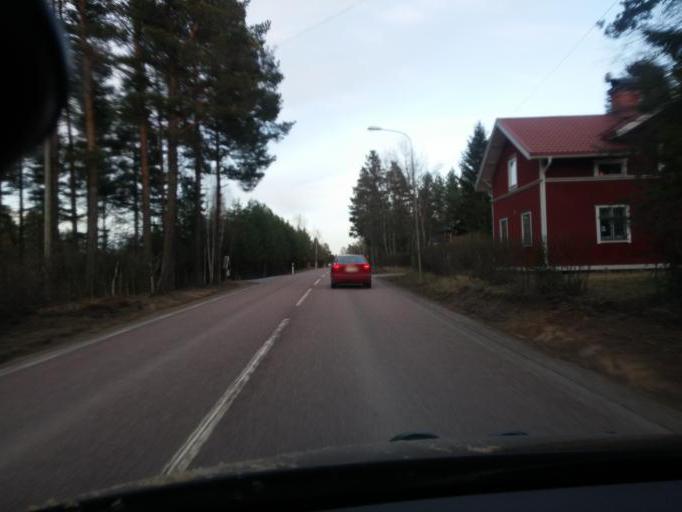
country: SE
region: Gaevleborg
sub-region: Ljusdals Kommun
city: Ljusdal
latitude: 61.8367
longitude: 16.0085
